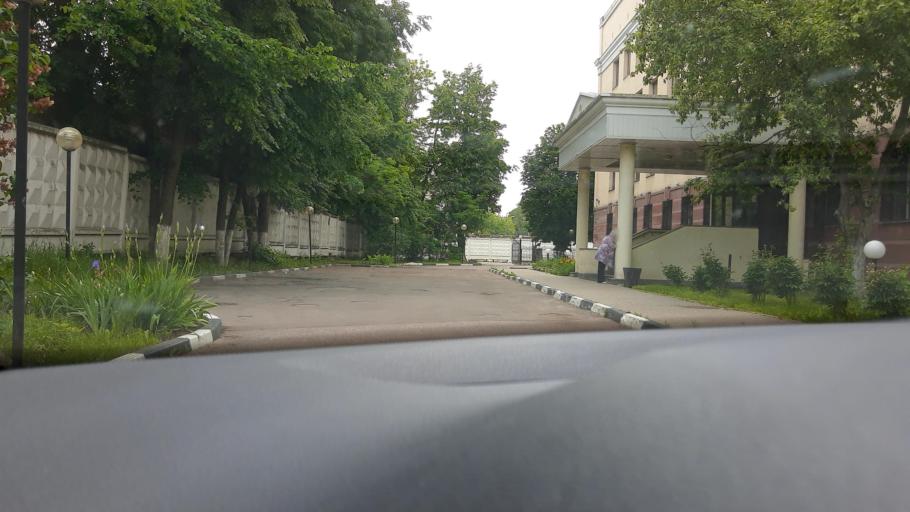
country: RU
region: Moskovskaya
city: Fili
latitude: 55.7537
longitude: 37.5001
